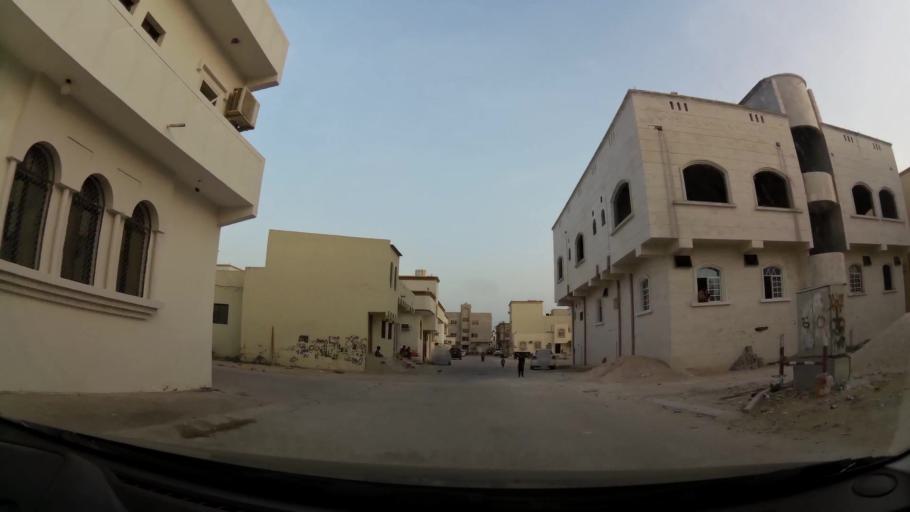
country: OM
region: Zufar
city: Salalah
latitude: 17.0225
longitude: 54.1274
